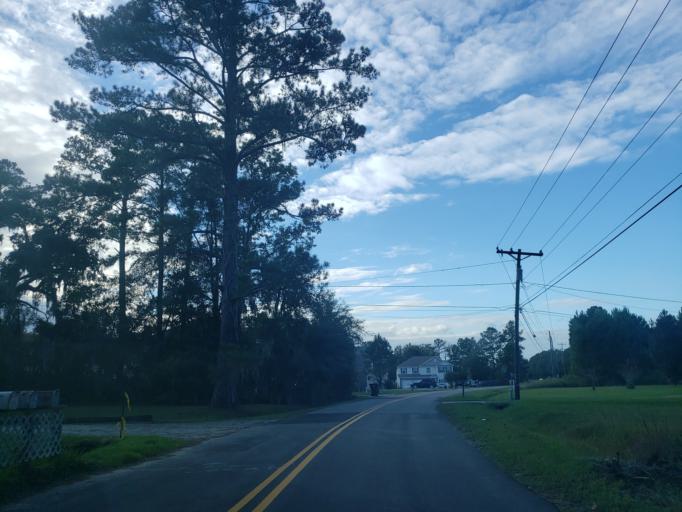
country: US
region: Georgia
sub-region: Chatham County
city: Georgetown
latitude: 31.9961
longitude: -81.2426
